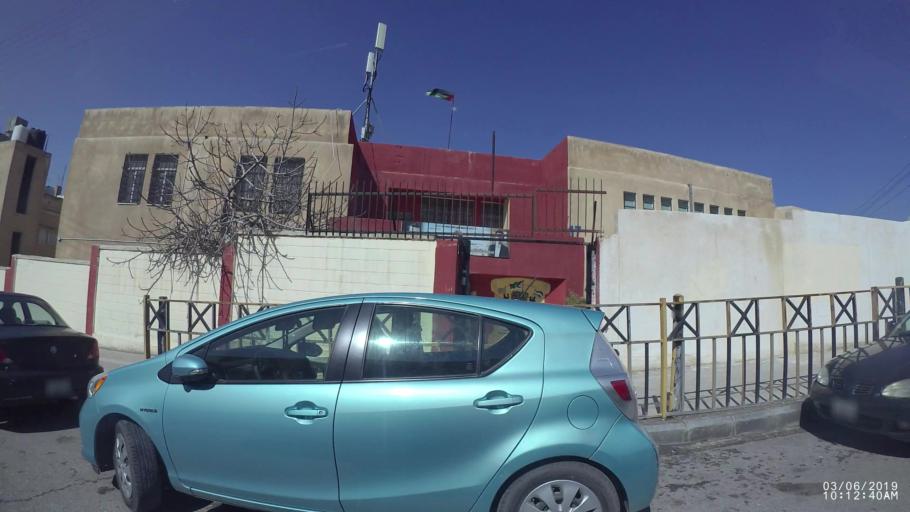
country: JO
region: Amman
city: Amman
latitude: 31.9818
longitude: 35.9852
